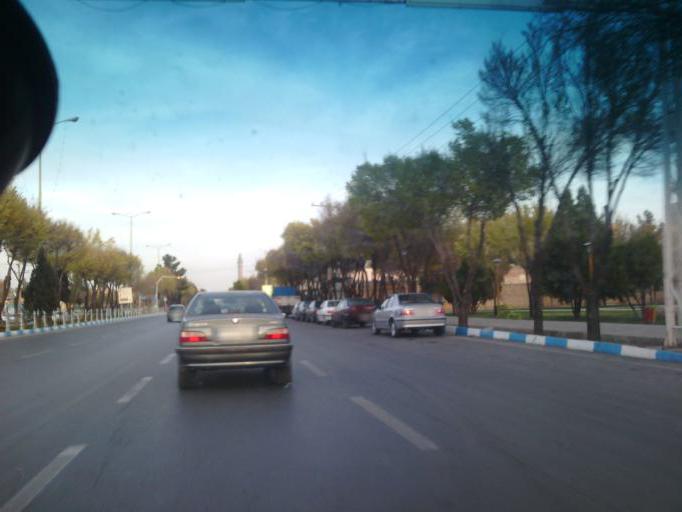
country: IR
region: Isfahan
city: Shahin Shahr
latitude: 32.8614
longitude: 51.5353
